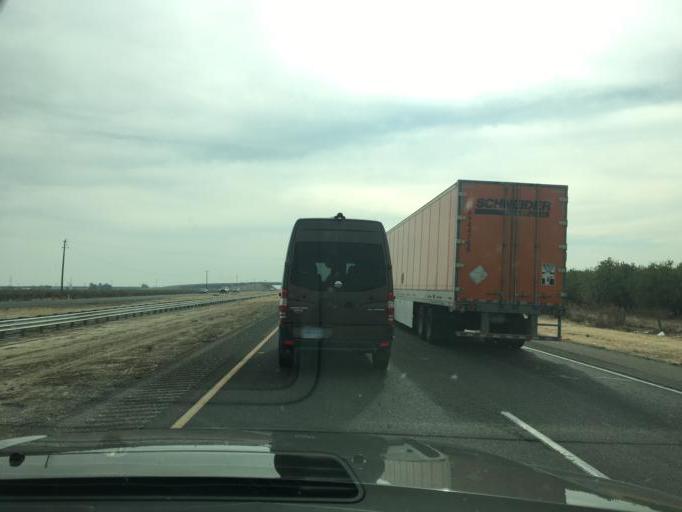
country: US
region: California
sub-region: Fresno County
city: Coalinga
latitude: 36.3742
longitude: -120.3393
